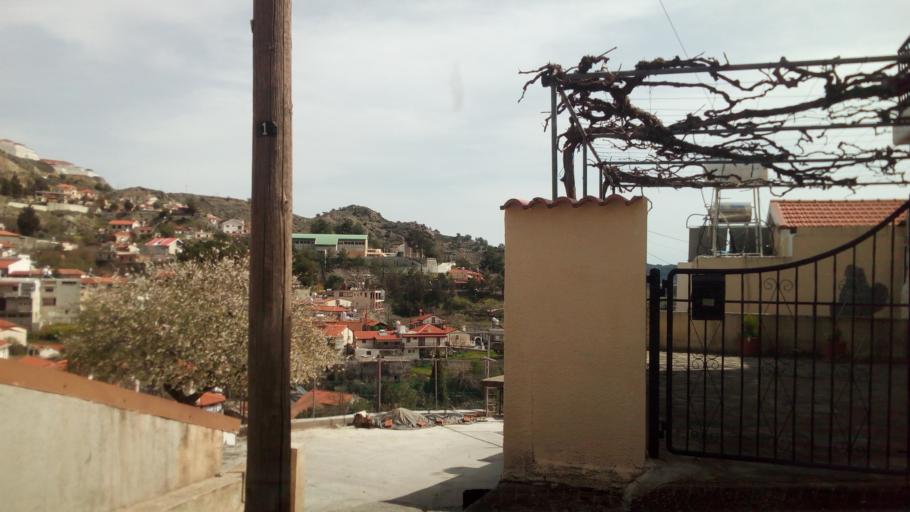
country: CY
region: Limassol
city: Pelendri
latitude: 34.8945
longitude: 32.9644
